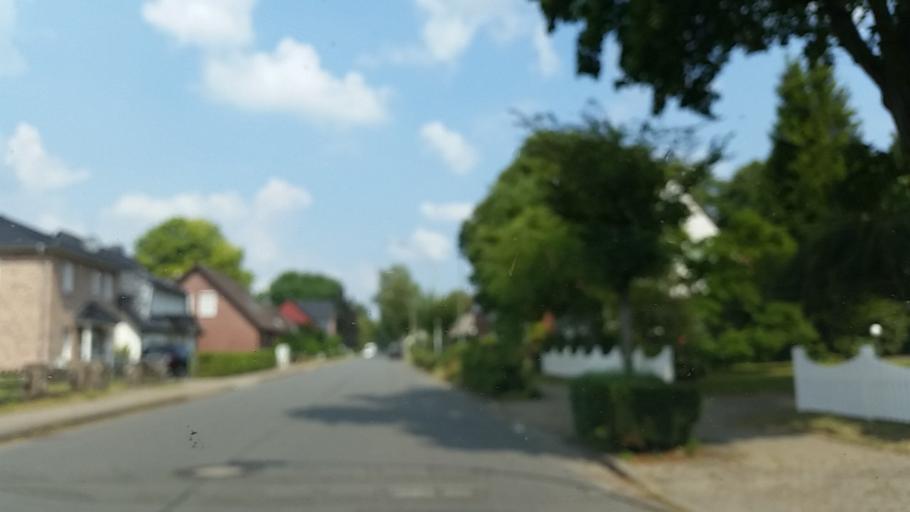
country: DE
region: Lower Saxony
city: Schneverdingen
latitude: 53.1226
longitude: 9.7885
